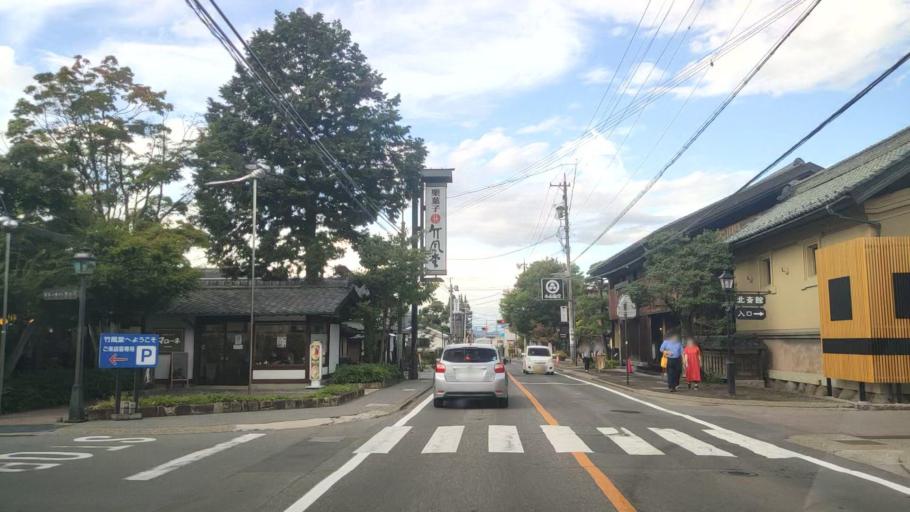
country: JP
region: Nagano
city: Suzaka
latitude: 36.6949
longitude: 138.3158
